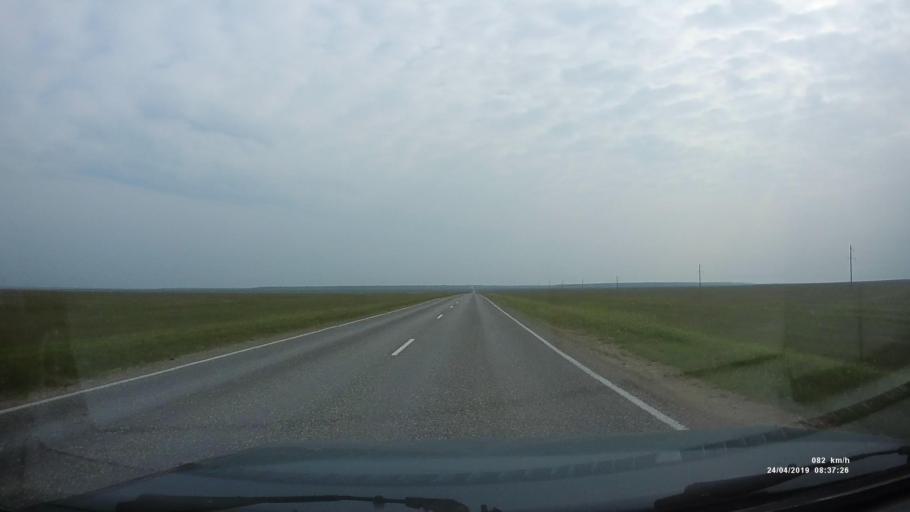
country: RU
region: Kalmykiya
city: Arshan'
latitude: 46.2100
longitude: 43.9508
